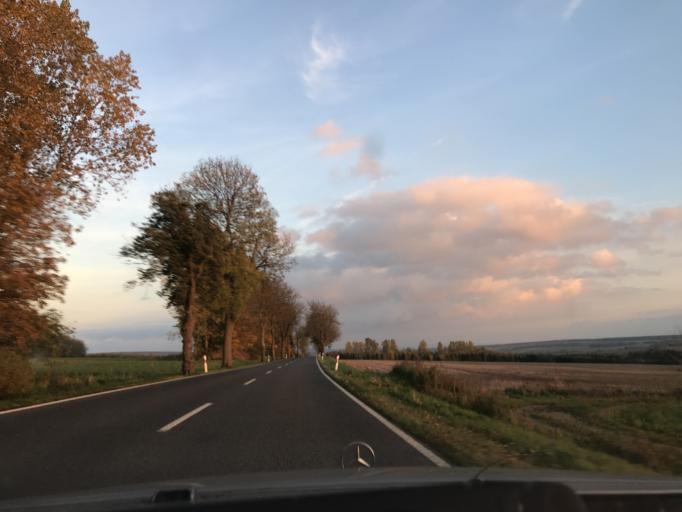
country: DE
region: Thuringia
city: Kefferhausen
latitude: 51.3363
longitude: 10.2752
